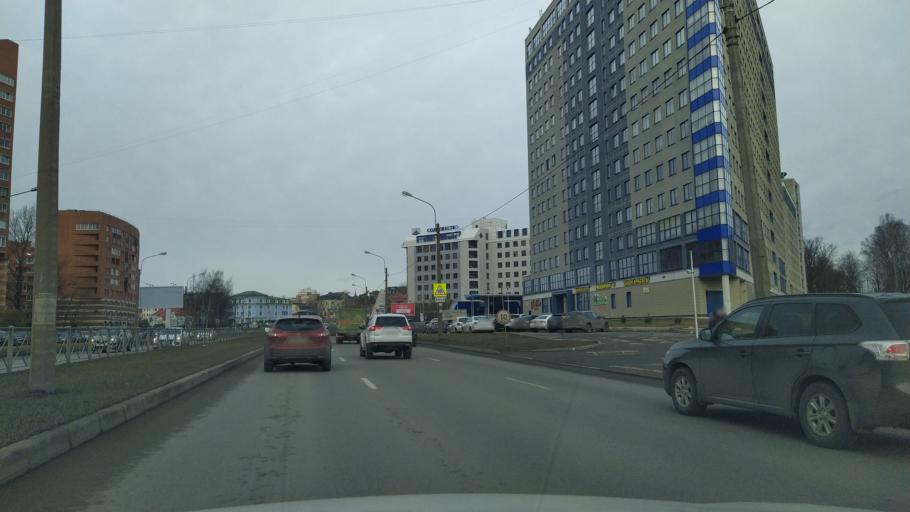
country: RU
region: St.-Petersburg
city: Kolomyagi
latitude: 60.0126
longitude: 30.2947
